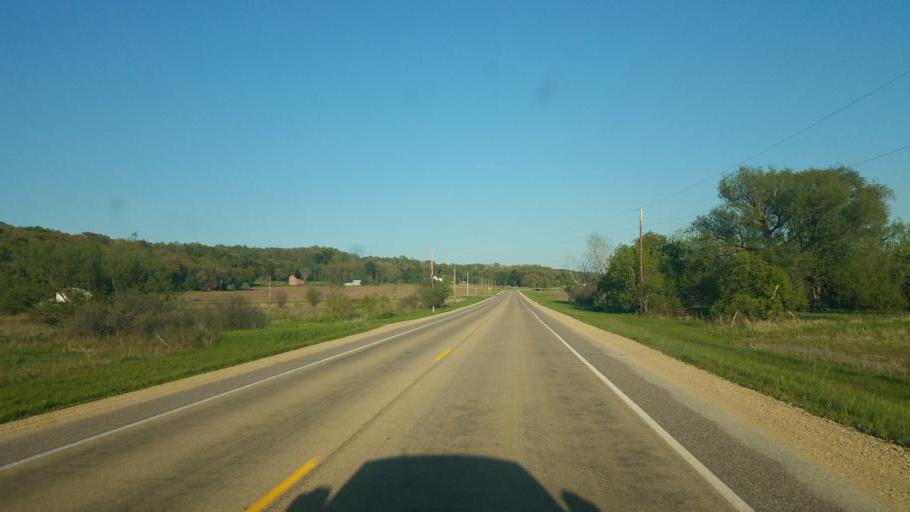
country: US
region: Wisconsin
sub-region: Sauk County
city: Reedsburg
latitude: 43.6187
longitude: -90.1512
